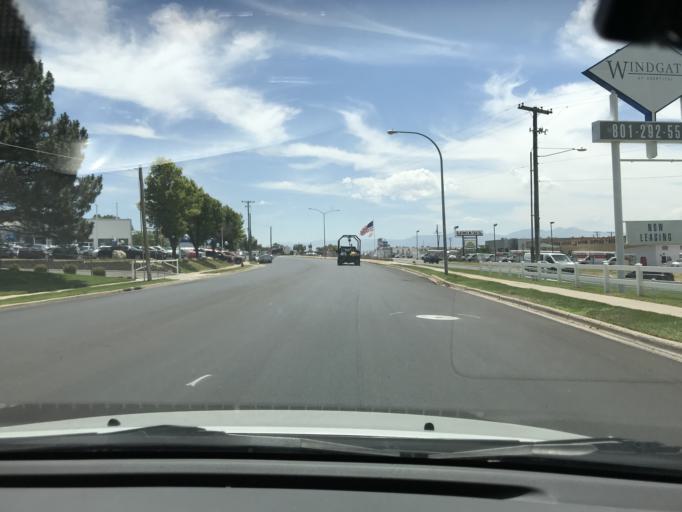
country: US
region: Utah
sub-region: Davis County
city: Woods Cross
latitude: 40.8676
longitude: -111.8916
